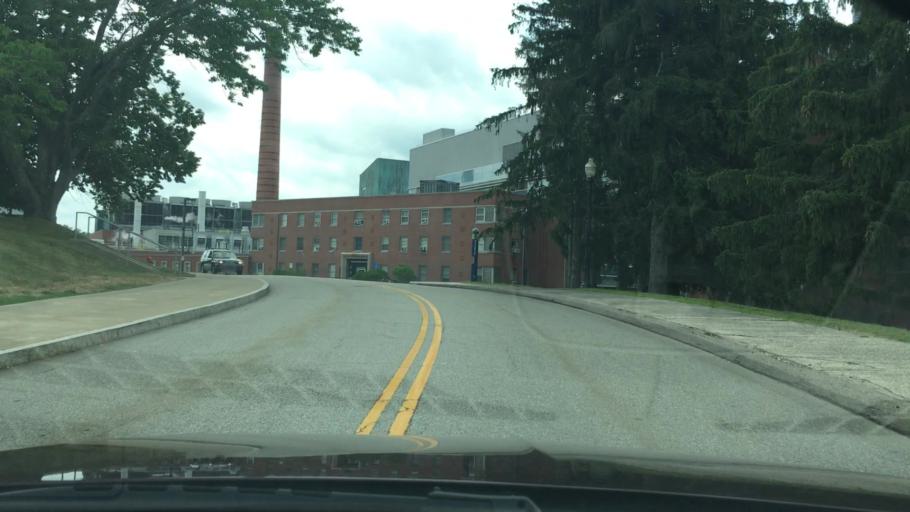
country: US
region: Connecticut
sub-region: Tolland County
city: Storrs
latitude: 41.8104
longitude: -72.2525
